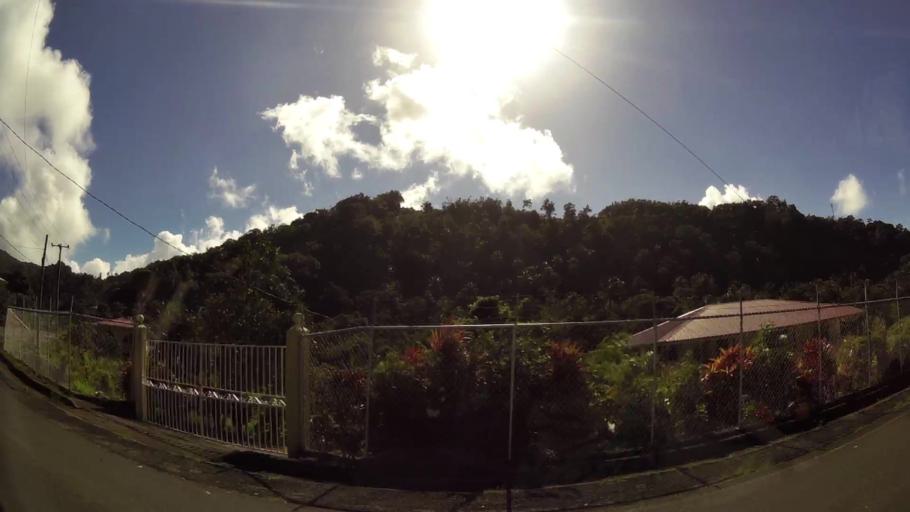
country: LC
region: Soufriere
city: Soufriere
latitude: 13.8188
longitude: -61.0382
